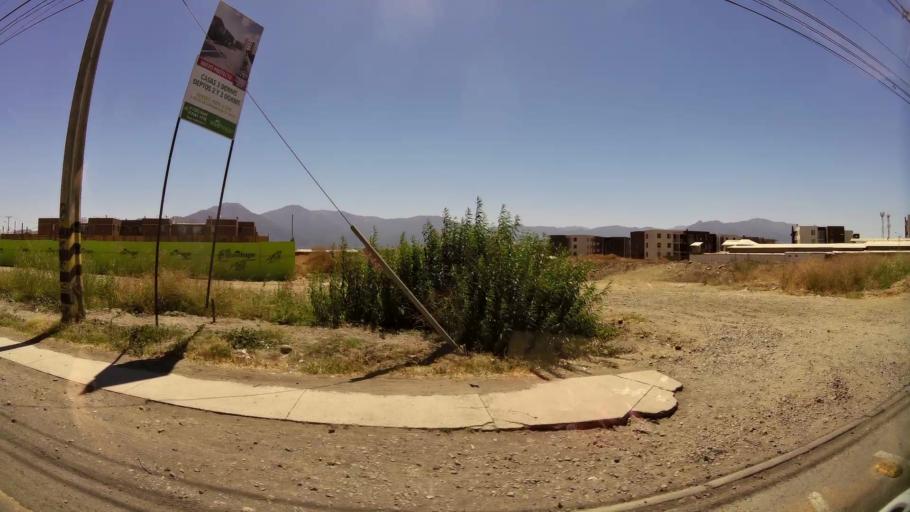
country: CL
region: O'Higgins
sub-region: Provincia de Cachapoal
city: Rancagua
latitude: -34.1729
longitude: -70.7786
